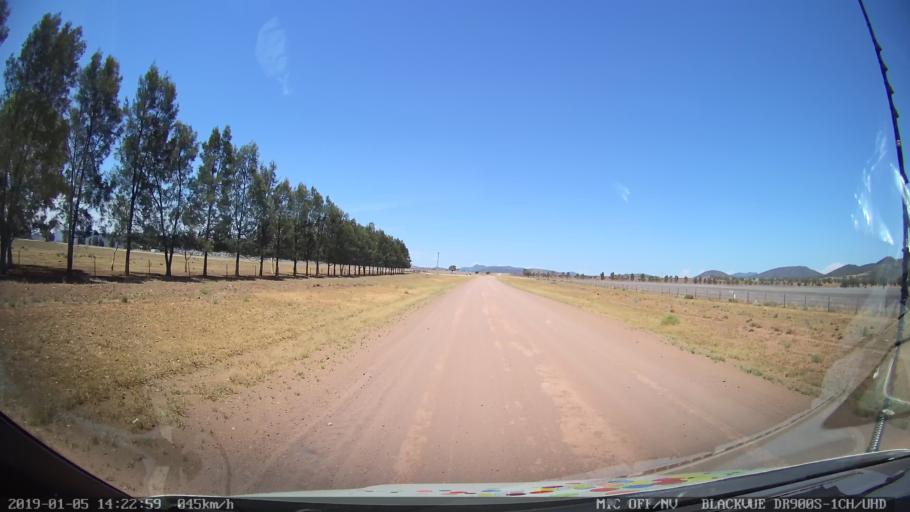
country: AU
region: New South Wales
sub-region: Liverpool Plains
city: Quirindi
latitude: -31.2430
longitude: 150.5274
